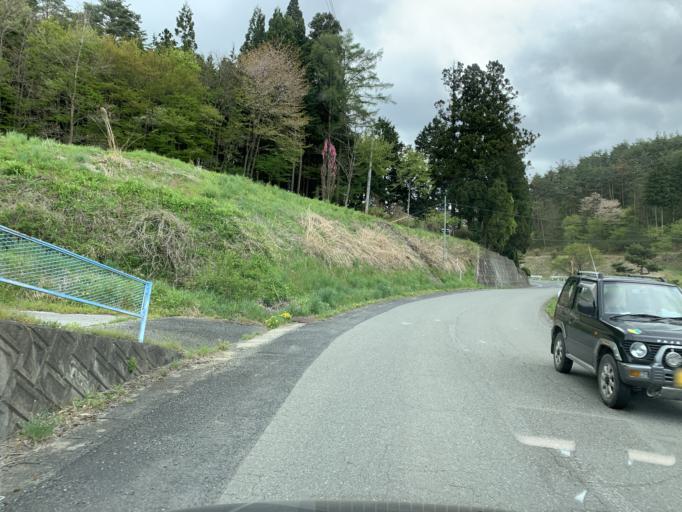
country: JP
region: Iwate
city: Ichinoseki
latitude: 38.8403
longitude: 141.3522
